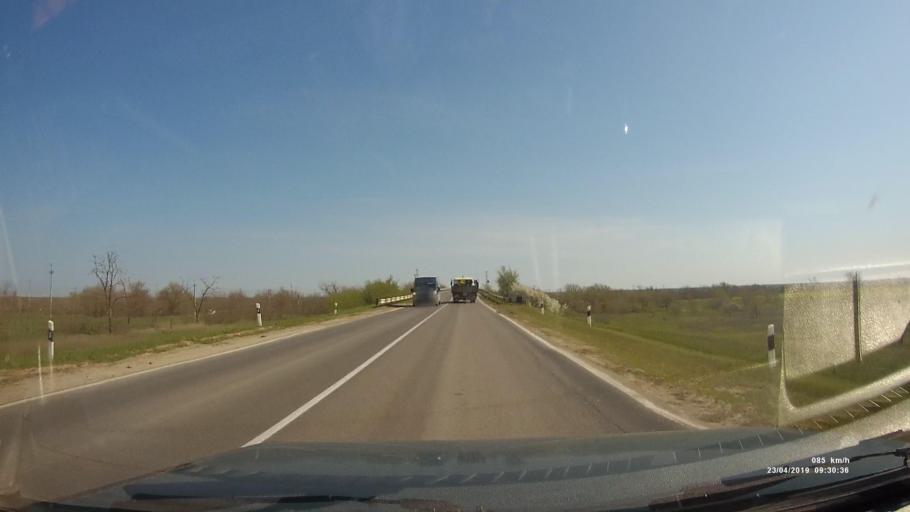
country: RU
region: Rostov
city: Gundorovskiy
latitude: 46.7730
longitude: 41.8180
